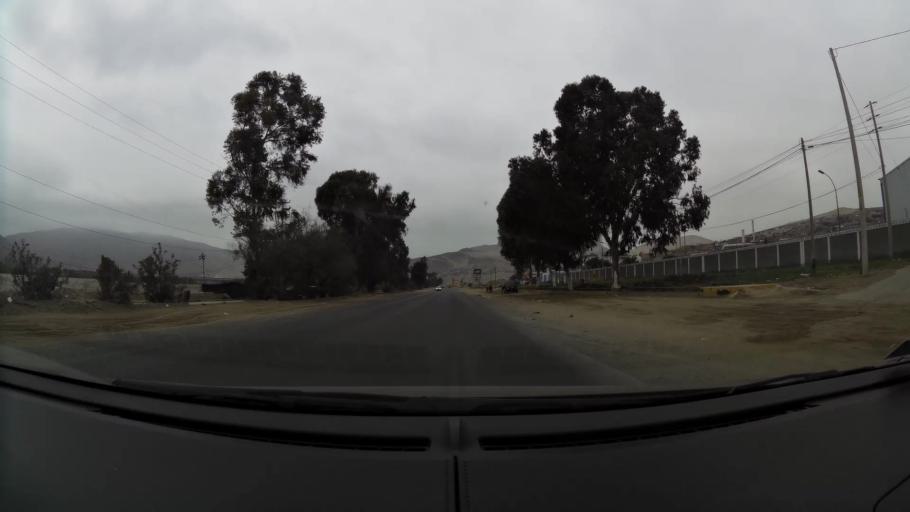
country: PE
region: Ancash
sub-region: Provincia de Santa
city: Chimbote
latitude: -9.0532
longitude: -78.5926
